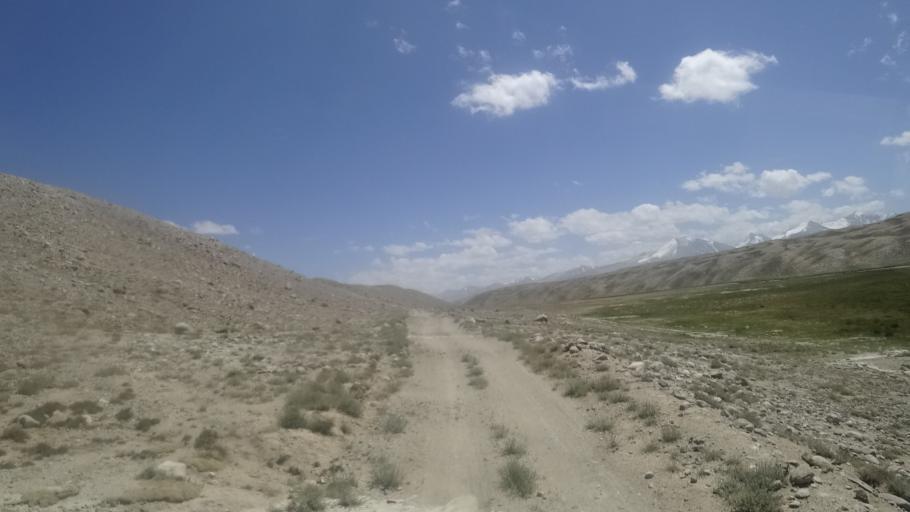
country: TJ
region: Gorno-Badakhshan
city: Murghob
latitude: 37.4649
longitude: 73.3485
